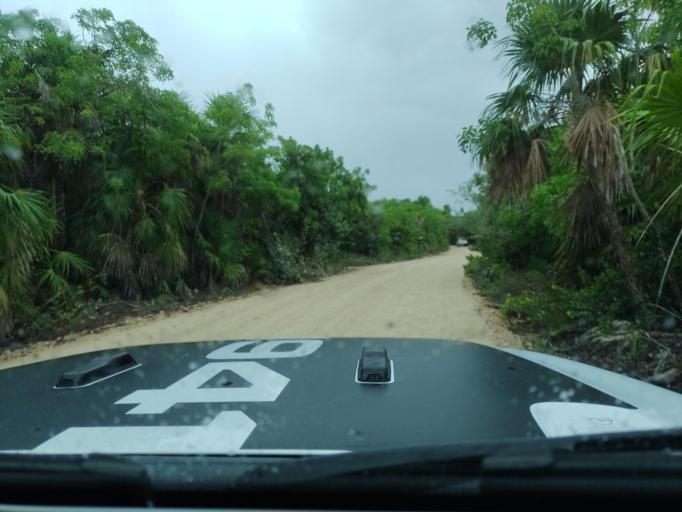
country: MX
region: Quintana Roo
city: Tulum
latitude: 20.0553
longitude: -87.4810
